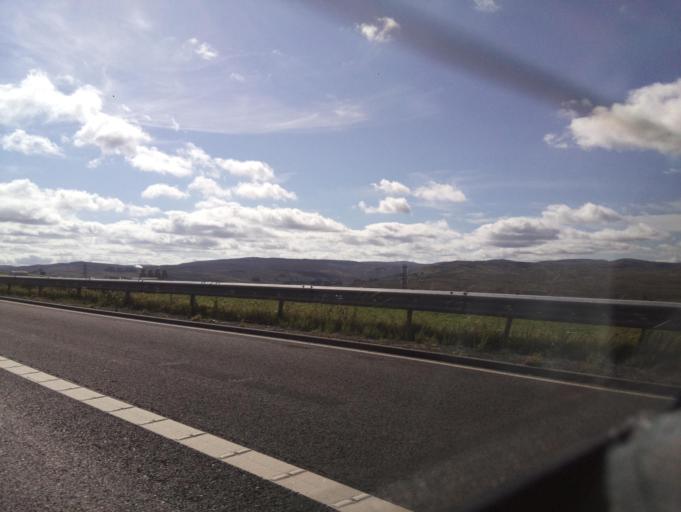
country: GB
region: England
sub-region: Cumbria
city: Penrith
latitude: 54.5228
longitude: -2.6590
